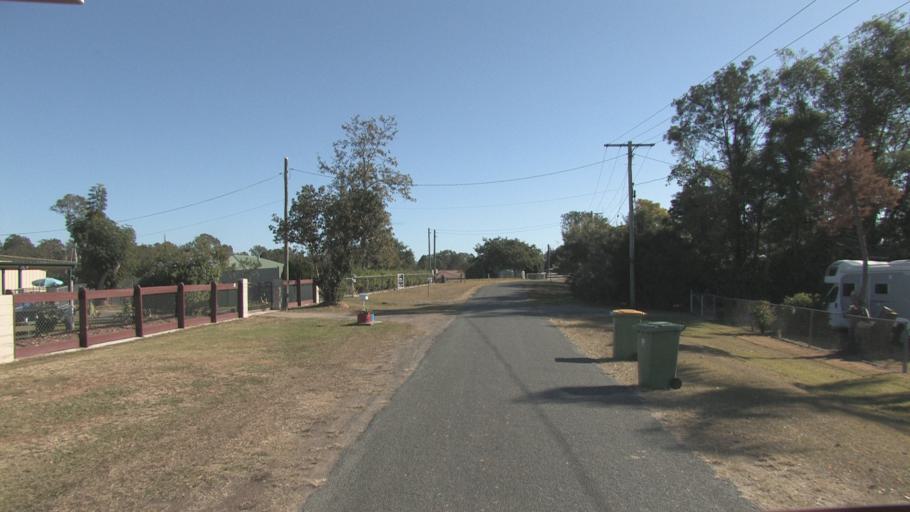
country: AU
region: Queensland
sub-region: Logan
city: North Maclean
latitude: -27.7834
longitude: 153.0027
